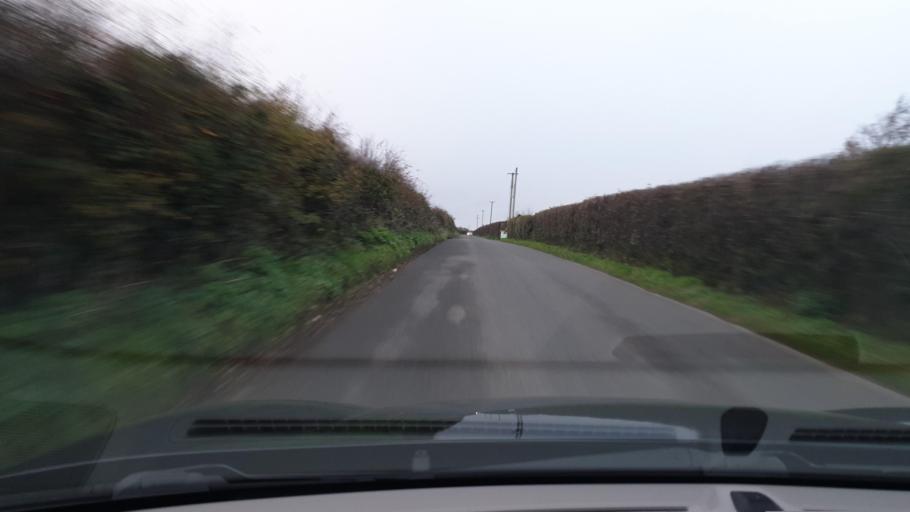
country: IE
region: Leinster
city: Lusk
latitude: 53.5542
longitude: -6.1551
